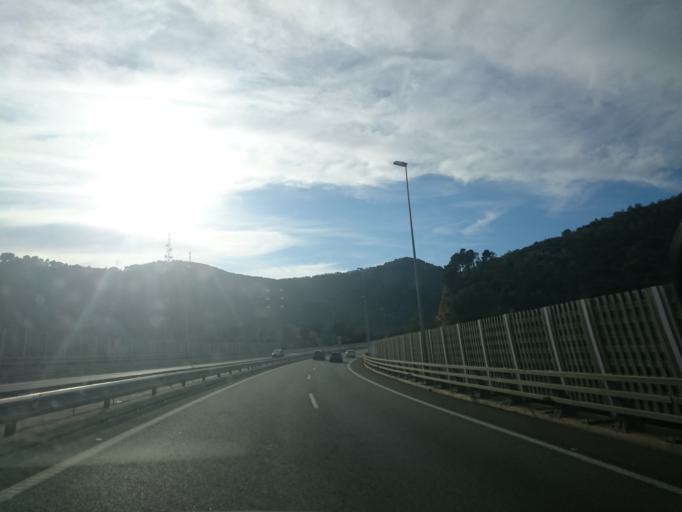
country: ES
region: Catalonia
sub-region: Provincia de Barcelona
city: Sitges
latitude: 41.2443
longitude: 1.8595
